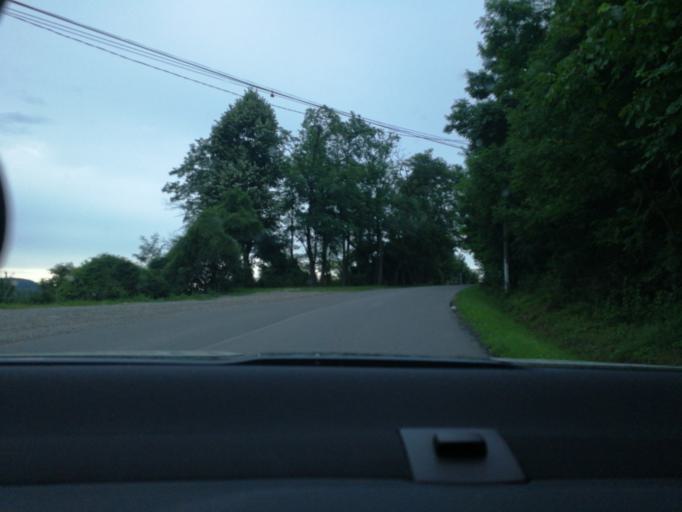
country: RO
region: Prahova
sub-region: Comuna Brebu
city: Brebu Megiesesc
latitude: 45.1500
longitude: 25.7725
